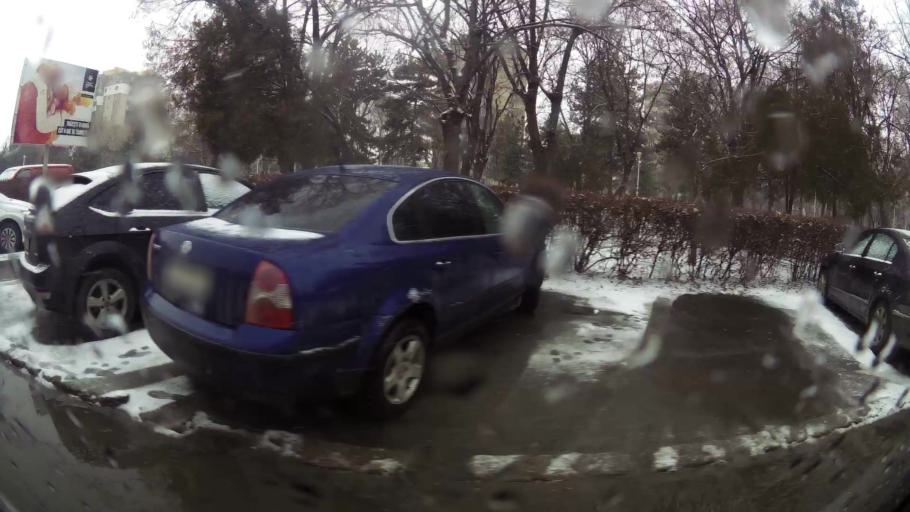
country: RO
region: Prahova
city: Ploiesti
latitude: 44.9351
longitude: 25.9866
